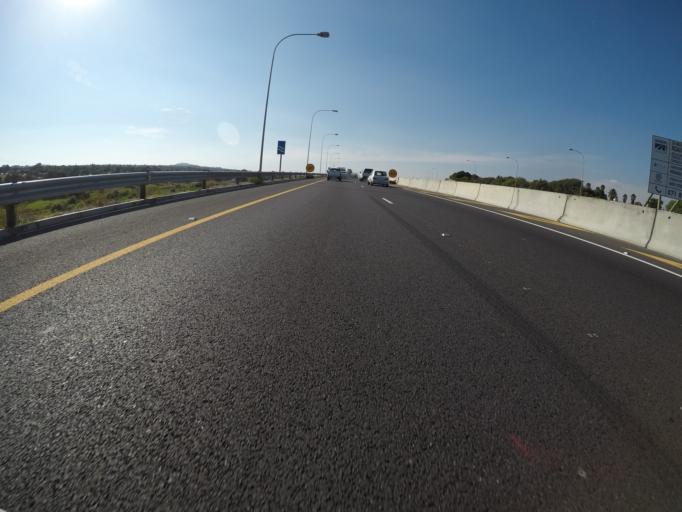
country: ZA
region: Western Cape
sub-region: City of Cape Town
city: Kraaifontein
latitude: -33.8787
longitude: 18.6728
